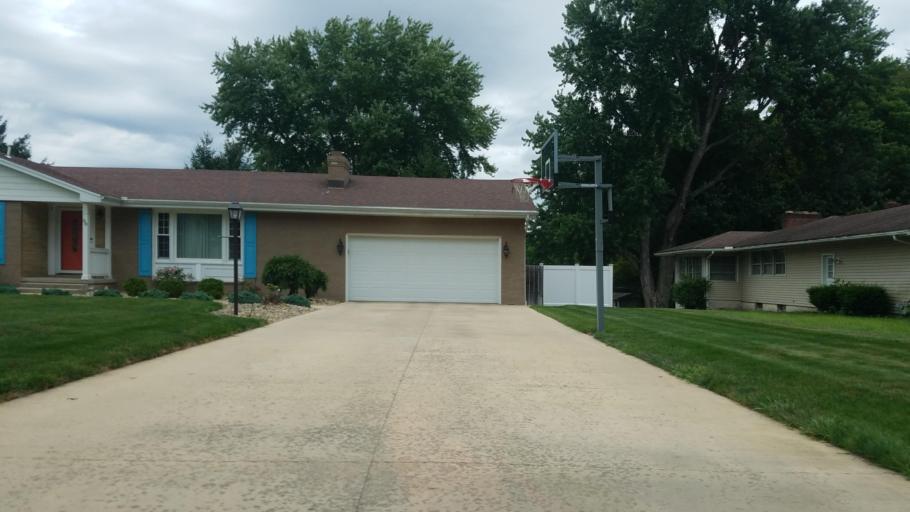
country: US
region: Ohio
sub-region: Mahoning County
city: Boardman
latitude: 41.0481
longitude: -80.7074
